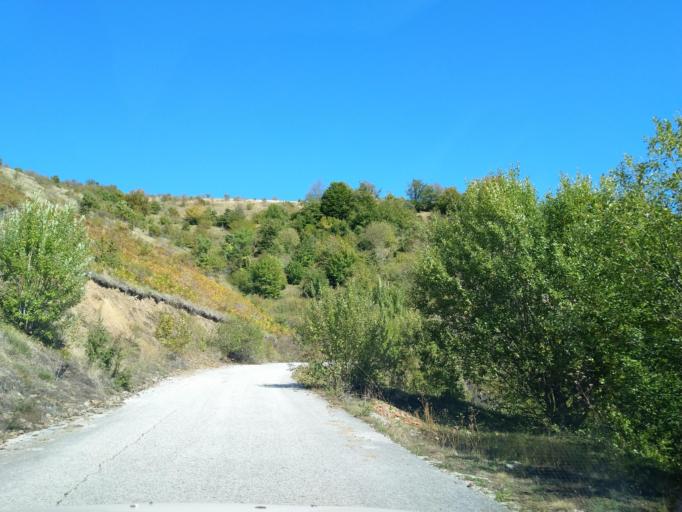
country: RS
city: Sokolovica
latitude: 43.2553
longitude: 20.3348
